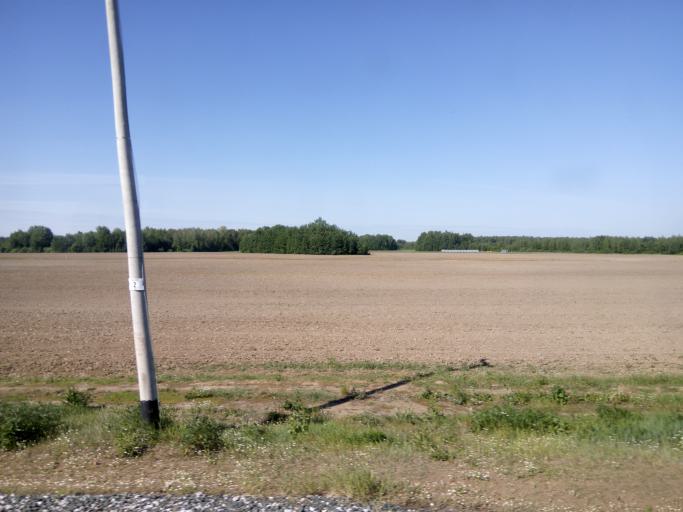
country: RU
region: Tatarstan
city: Stolbishchi
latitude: 55.6807
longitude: 49.2050
